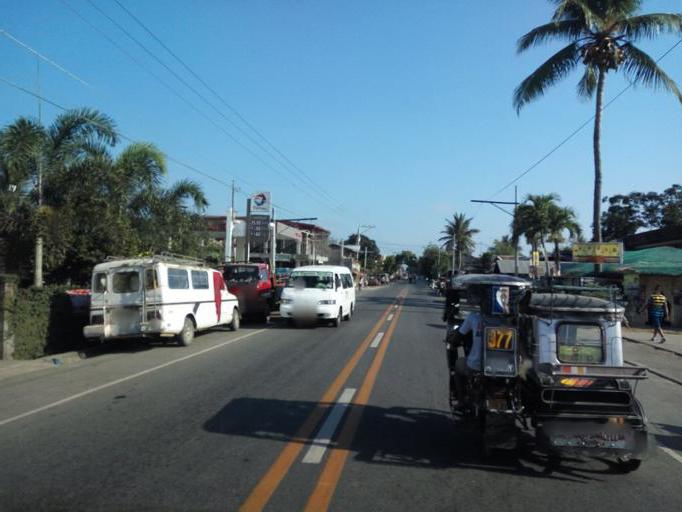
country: PH
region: Cagayan Valley
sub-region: Province of Cagayan
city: Amulung
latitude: 17.8389
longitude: 121.7230
